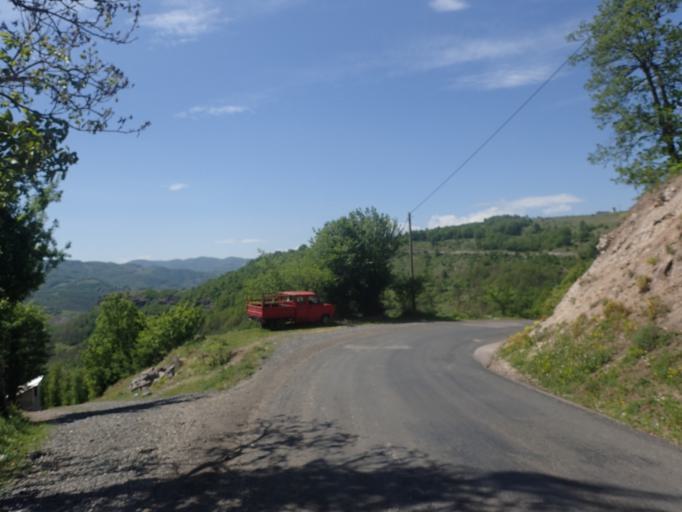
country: TR
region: Ordu
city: Akkus
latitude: 40.7984
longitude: 36.9386
